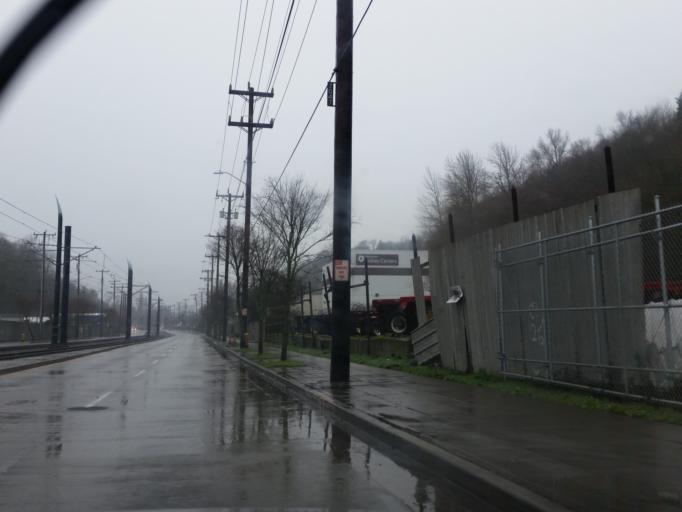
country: US
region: Washington
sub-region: King County
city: Riverton
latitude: 47.5138
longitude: -122.2787
